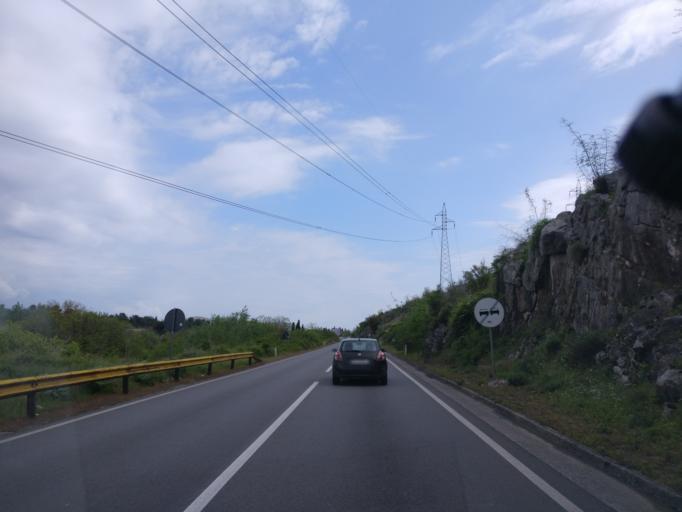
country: ME
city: Spuz
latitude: 42.4473
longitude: 19.2017
